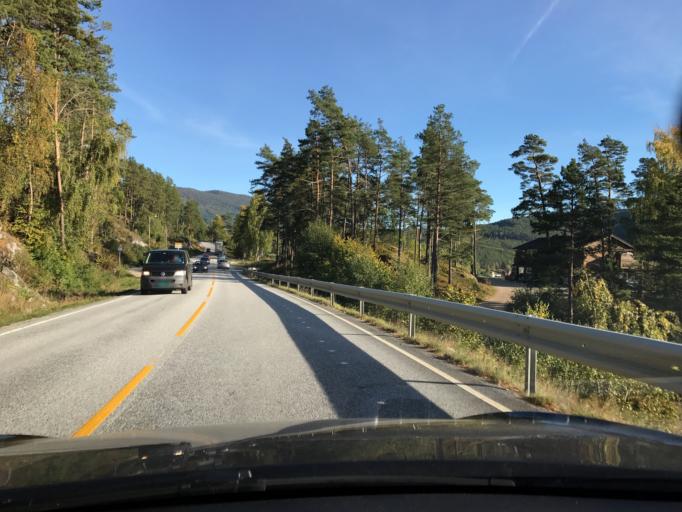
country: NO
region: Sogn og Fjordane
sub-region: Sogndal
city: Sogndalsfjora
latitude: 61.2067
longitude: 7.1648
